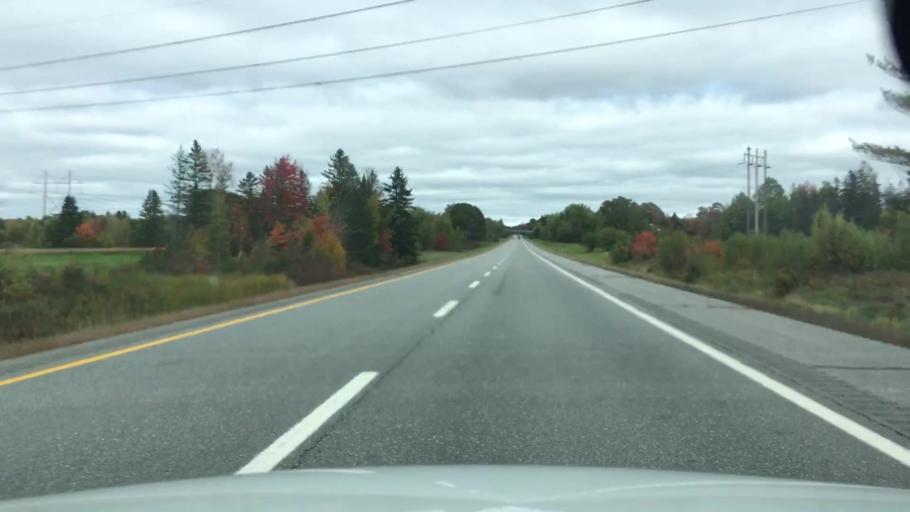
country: US
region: Maine
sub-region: Kennebec County
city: Clinton
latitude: 44.6561
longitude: -69.5061
